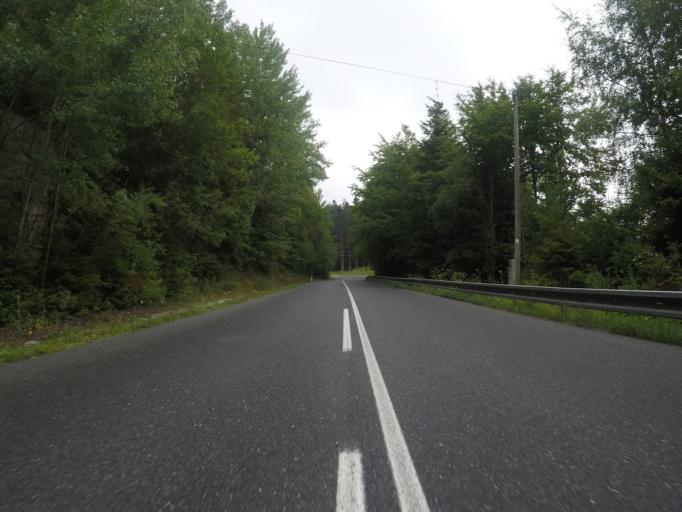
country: SK
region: Kosicky
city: Spisska Nova Ves
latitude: 48.8732
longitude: 20.5264
